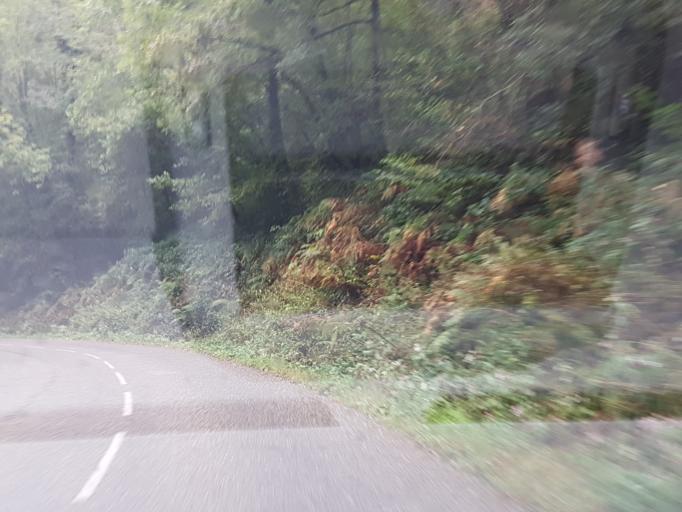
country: FR
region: Midi-Pyrenees
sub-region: Departement de l'Ariege
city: Saint-Girons
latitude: 42.9137
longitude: 1.2596
